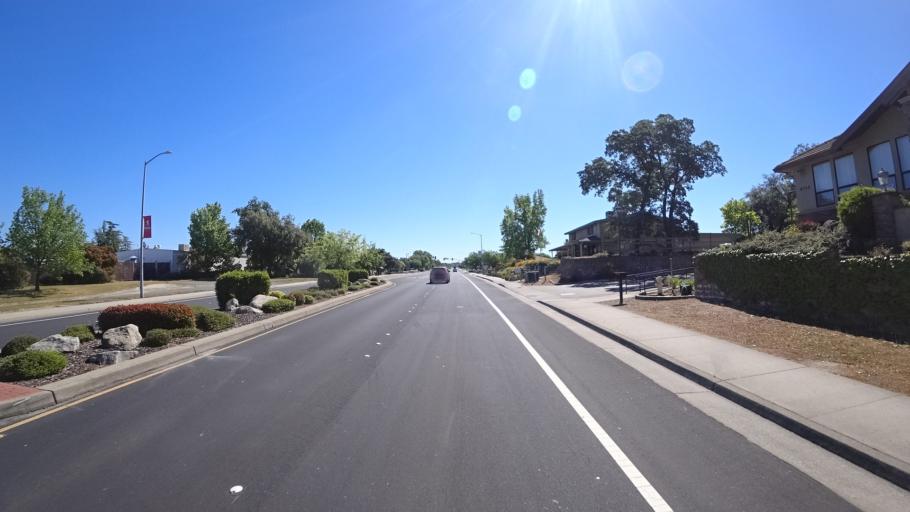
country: US
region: California
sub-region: Placer County
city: Rocklin
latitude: 38.7884
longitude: -121.2172
